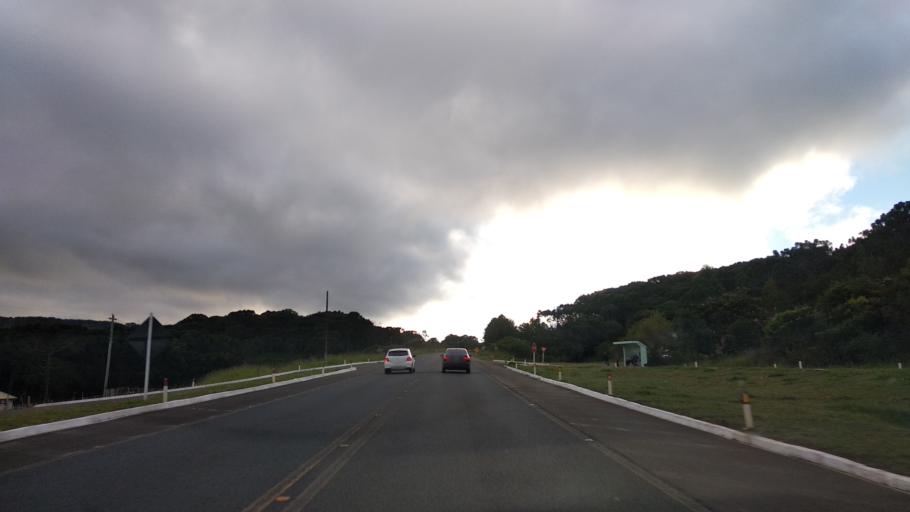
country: BR
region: Santa Catarina
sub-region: Curitibanos
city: Curitibanos
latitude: -27.5790
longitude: -50.7714
